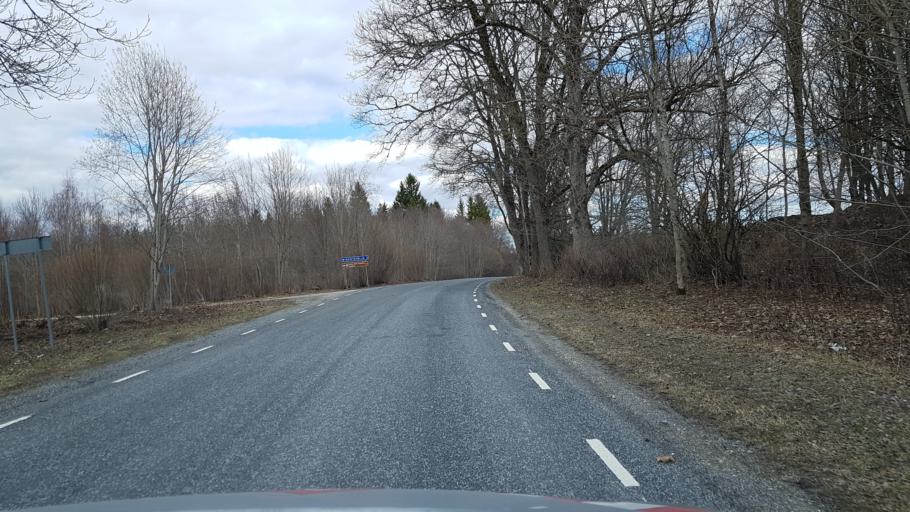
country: EE
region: Laeaene-Virumaa
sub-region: Tamsalu vald
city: Tamsalu
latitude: 59.1839
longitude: 26.1278
